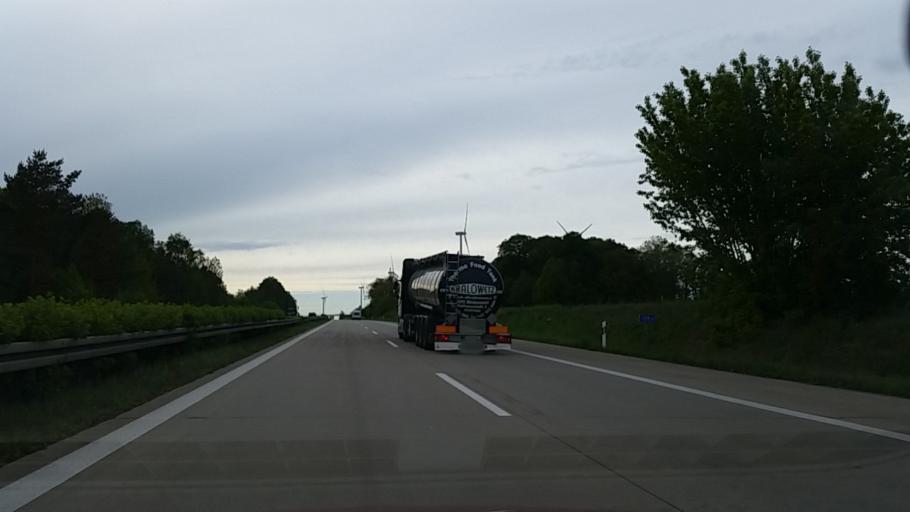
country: DE
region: Brandenburg
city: Putlitz
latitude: 53.2944
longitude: 12.0351
